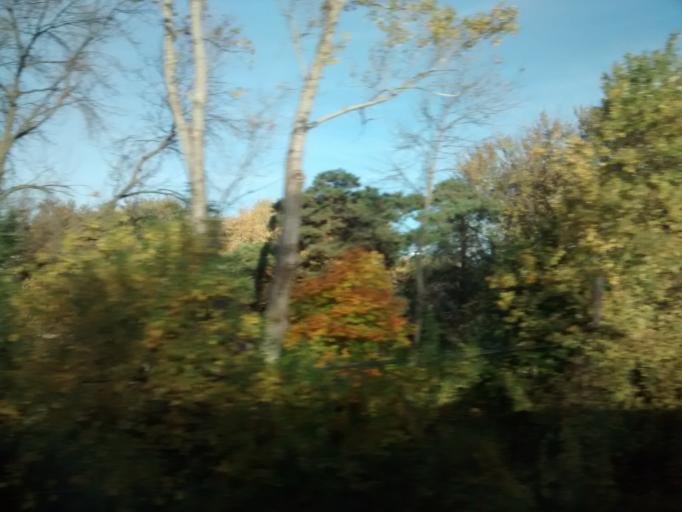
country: CA
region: Ontario
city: Etobicoke
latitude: 43.5855
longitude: -79.5549
